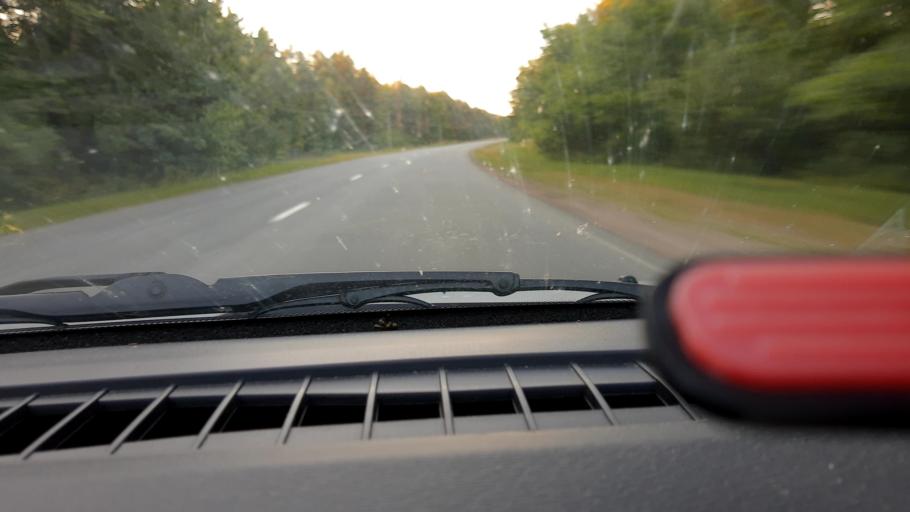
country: RU
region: Nizjnij Novgorod
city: Uren'
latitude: 57.4109
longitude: 45.6839
